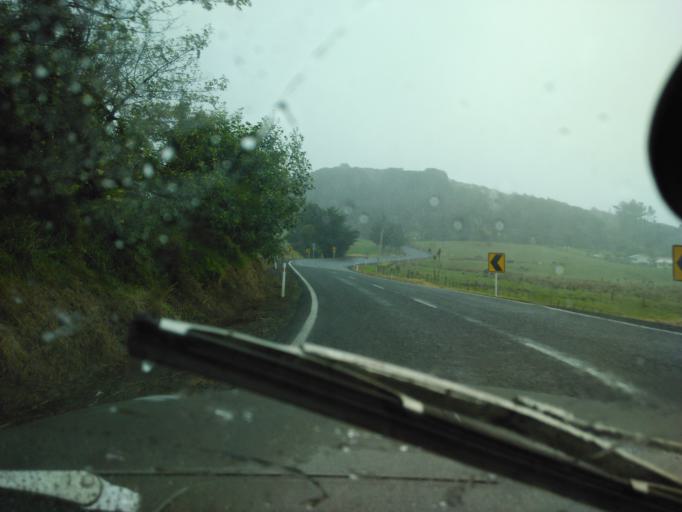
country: NZ
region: Auckland
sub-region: Auckland
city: Wellsford
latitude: -36.4316
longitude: 174.4386
